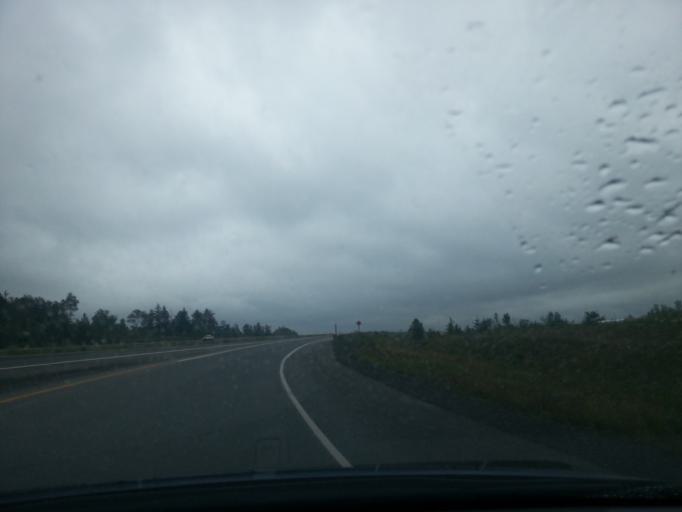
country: CA
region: New Brunswick
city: Fredericton
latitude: 45.9265
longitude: -66.7140
